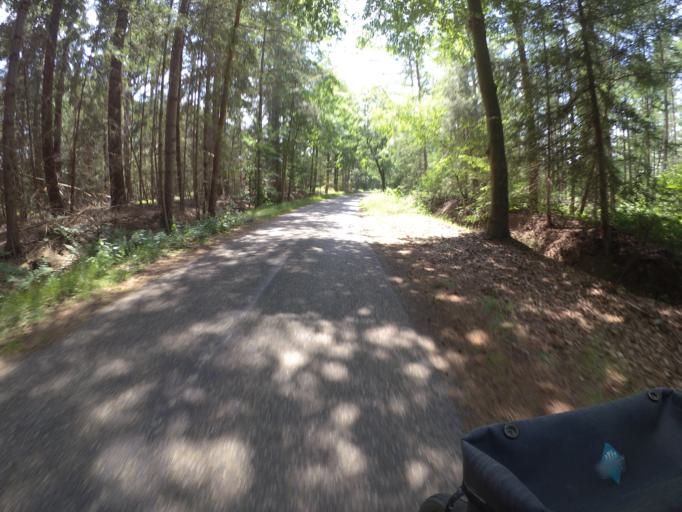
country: NL
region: North Brabant
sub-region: Gemeente Oirschot
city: Middelbeers
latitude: 51.4935
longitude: 5.2485
